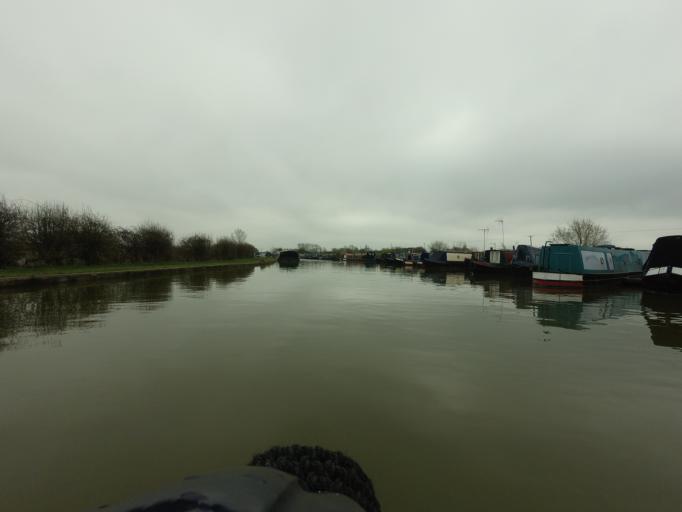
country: GB
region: England
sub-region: Central Bedfordshire
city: Leighton Buzzard
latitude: 51.8976
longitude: -0.6709
